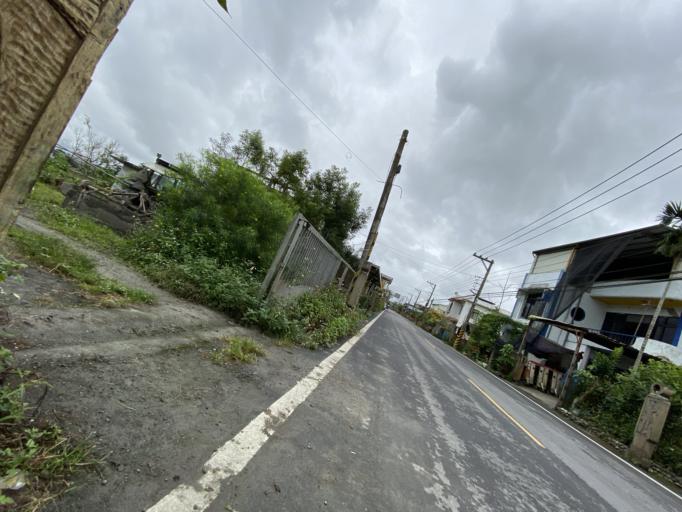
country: TW
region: Taiwan
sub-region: Hualien
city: Hualian
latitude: 23.6569
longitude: 121.4522
